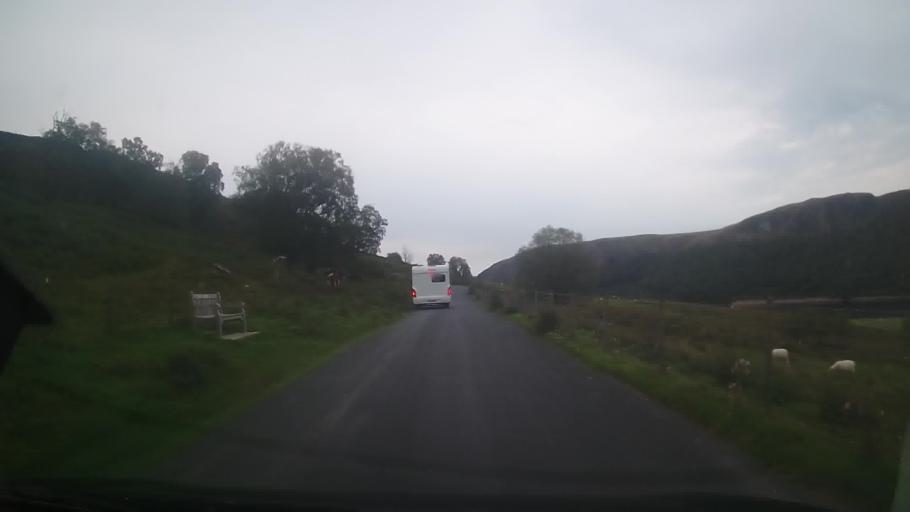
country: GB
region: Wales
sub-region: Sir Powys
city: Rhayader
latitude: 52.2937
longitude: -3.6163
